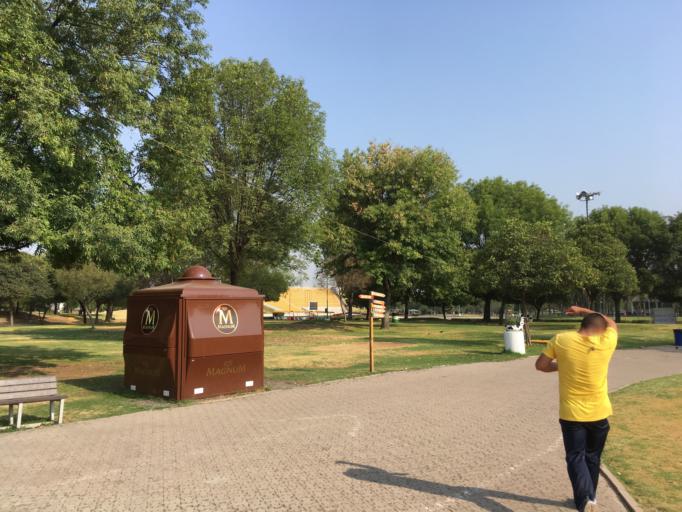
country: MX
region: Guanajuato
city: Leon
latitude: 21.1102
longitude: -101.6591
